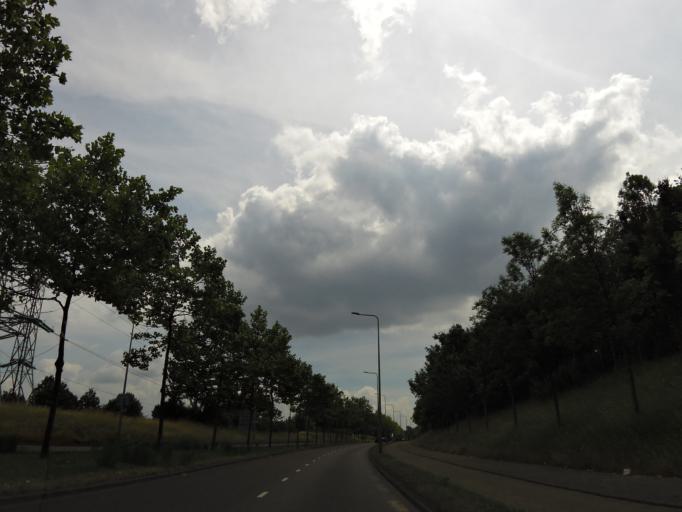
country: NL
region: Limburg
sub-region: Gemeente Heerlen
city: Heerlen
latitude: 50.9008
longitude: 5.9641
